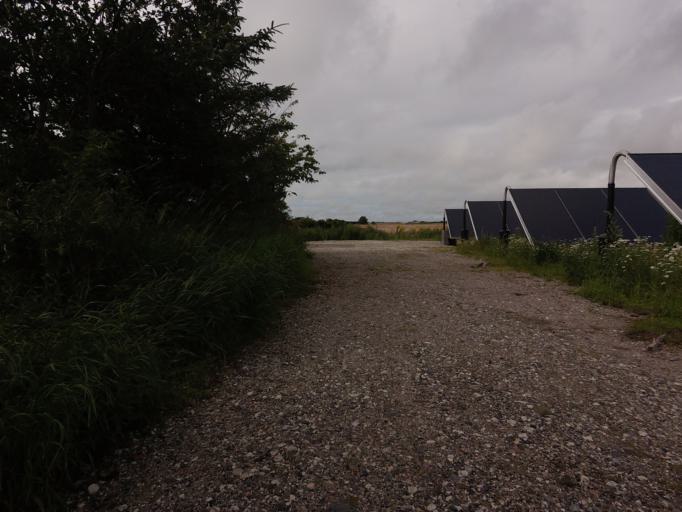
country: DK
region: North Denmark
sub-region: Jammerbugt Kommune
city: Pandrup
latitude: 57.3708
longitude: 9.7346
